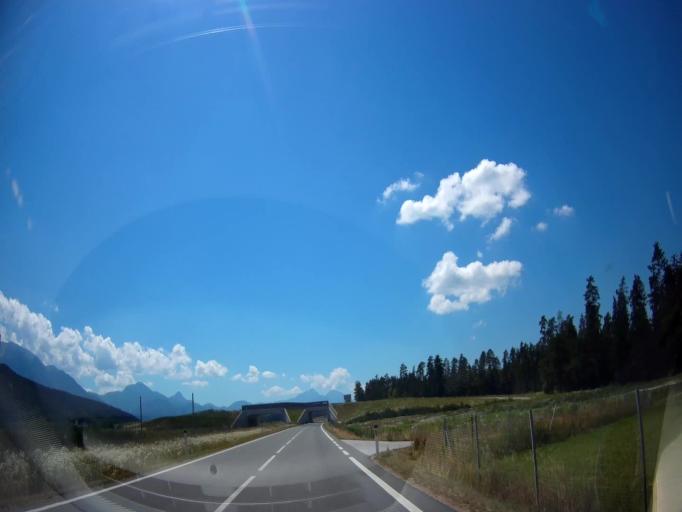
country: AT
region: Carinthia
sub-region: Politischer Bezirk Volkermarkt
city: Bleiburg/Pliberk
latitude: 46.6067
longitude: 14.7757
